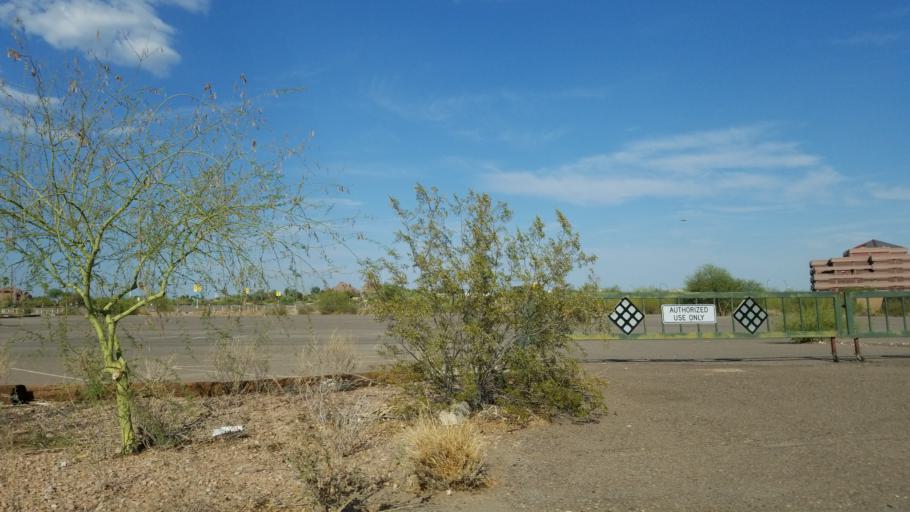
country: US
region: Arizona
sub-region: Maricopa County
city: Tempe Junction
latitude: 33.4494
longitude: -111.9610
